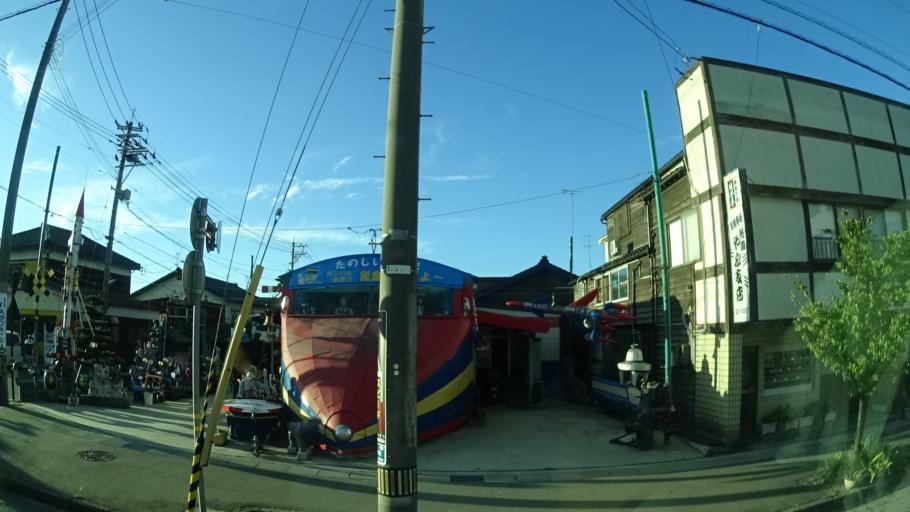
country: JP
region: Ishikawa
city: Nanao
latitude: 37.3911
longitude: 136.9010
